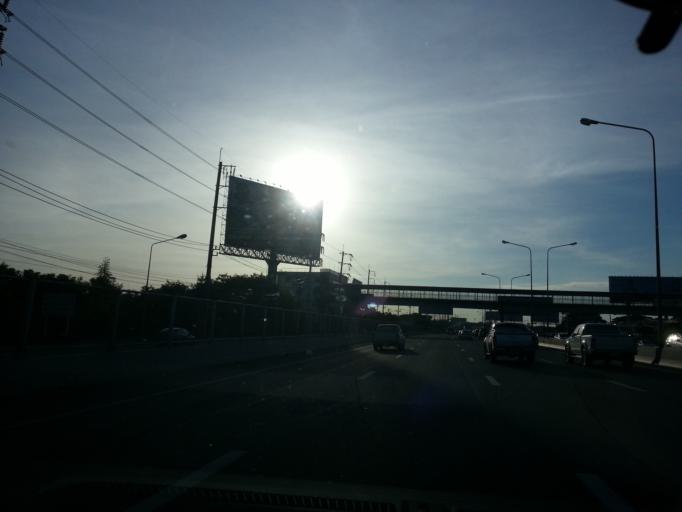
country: TH
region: Bangkok
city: Suan Luang
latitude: 13.7394
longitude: 100.6523
